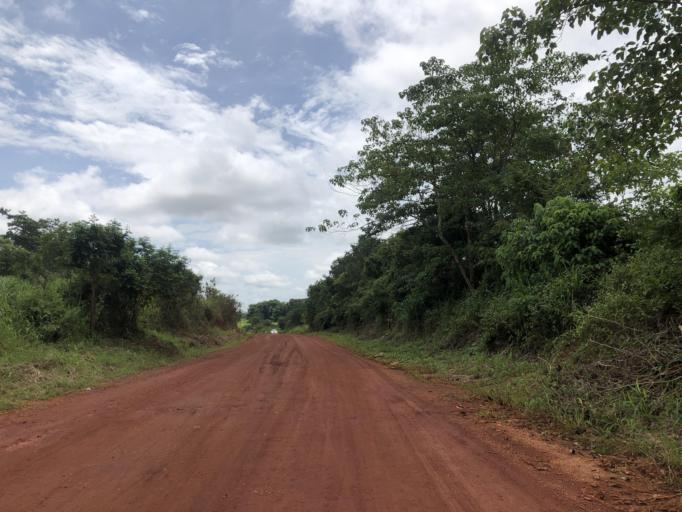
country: SL
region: Northern Province
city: Lunsar
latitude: 8.6700
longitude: -12.5266
